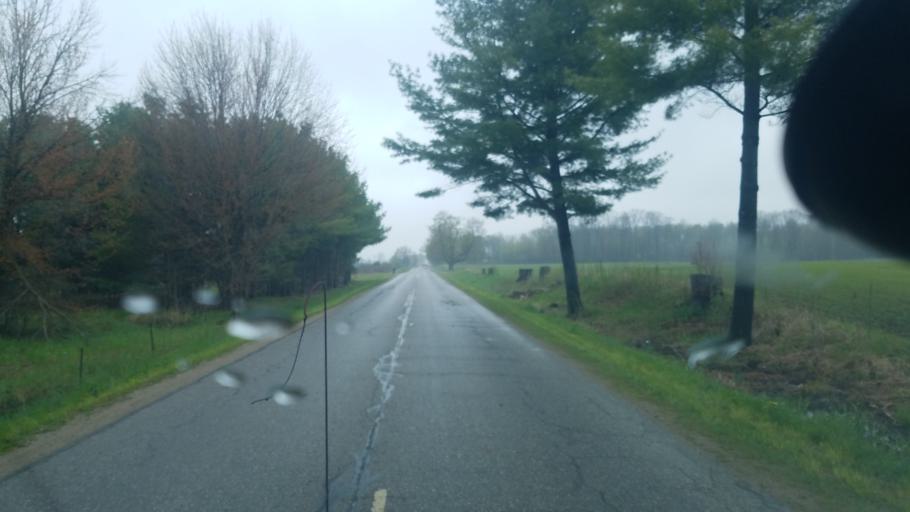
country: US
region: Michigan
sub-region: Montcalm County
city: Lakeview
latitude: 43.4996
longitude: -85.2842
